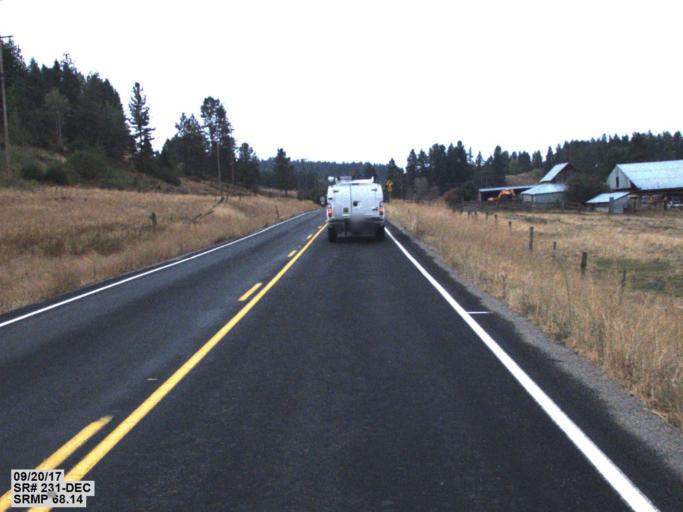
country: US
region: Washington
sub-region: Stevens County
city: Chewelah
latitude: 48.1274
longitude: -117.7441
